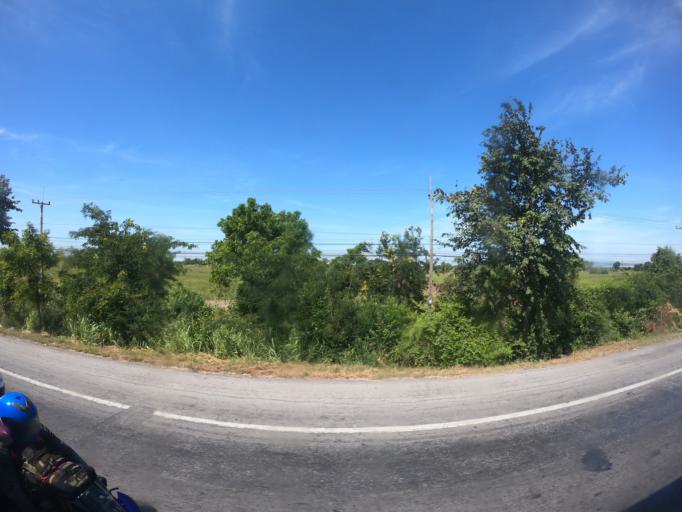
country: TH
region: Nakhon Ratchasima
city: Non Sung
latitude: 15.2160
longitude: 102.3591
